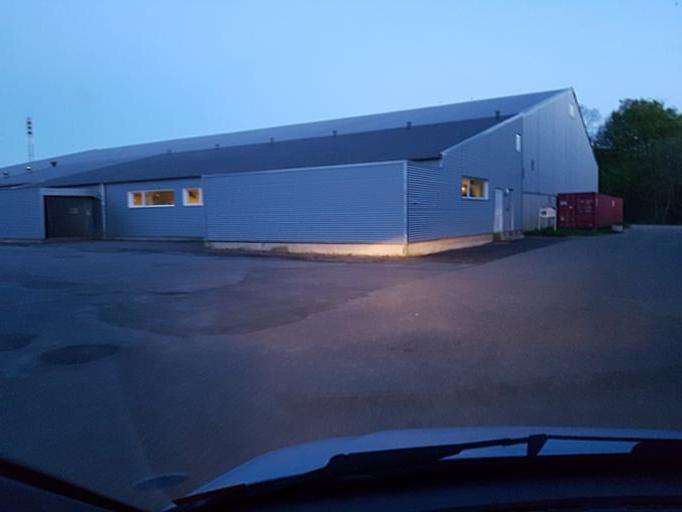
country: DK
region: South Denmark
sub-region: Esbjerg Kommune
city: Esbjerg
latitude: 55.4831
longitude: 8.4359
